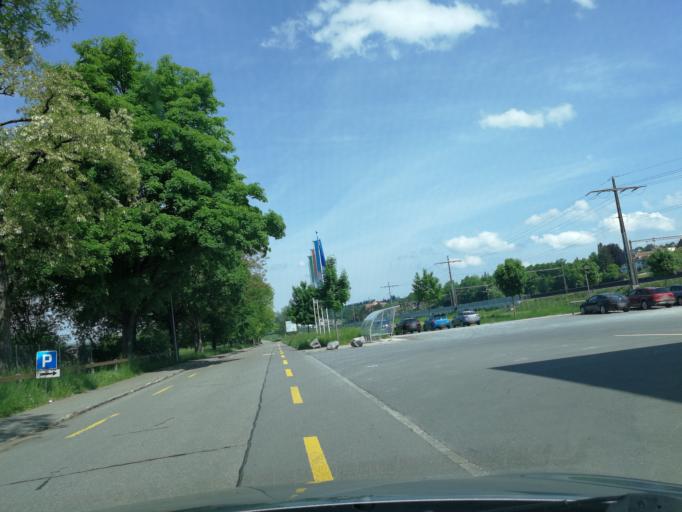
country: CH
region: Bern
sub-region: Bern-Mittelland District
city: Munsingen
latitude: 46.8756
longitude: 7.5576
